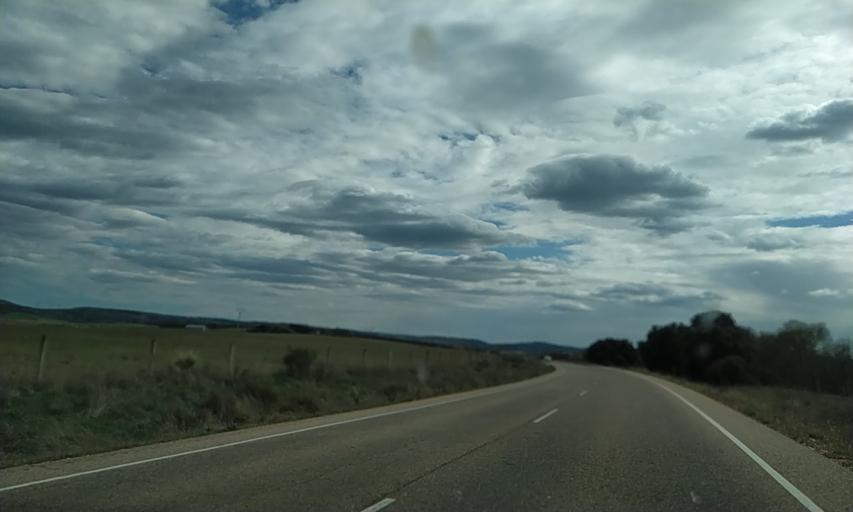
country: ES
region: Castille and Leon
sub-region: Provincia de Salamanca
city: Pastores
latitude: 40.5421
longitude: -6.5637
